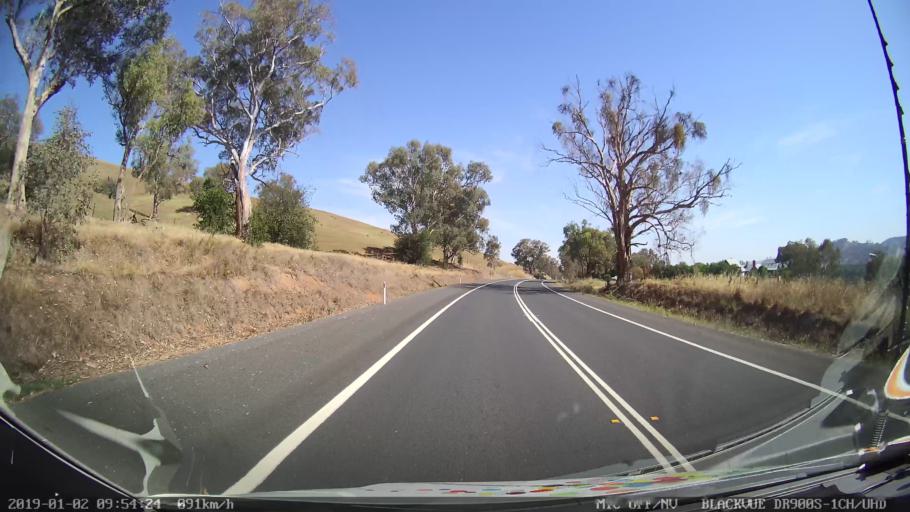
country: AU
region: New South Wales
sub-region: Tumut Shire
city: Tumut
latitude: -35.2358
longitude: 148.1965
